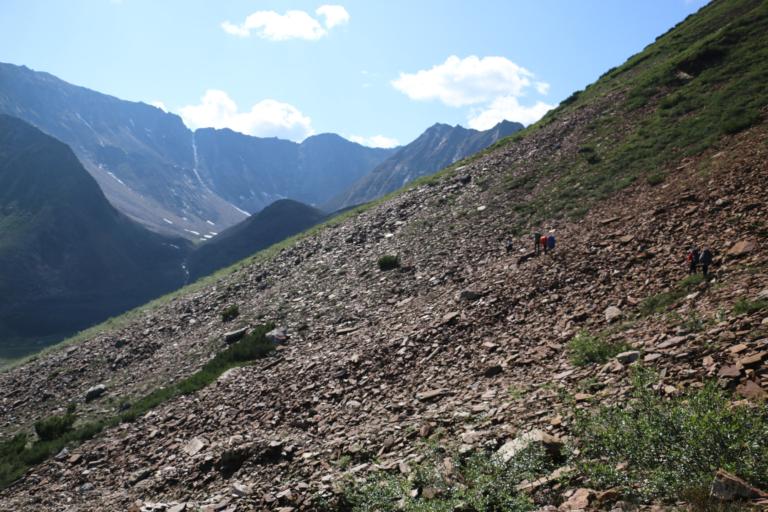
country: RU
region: Respublika Buryatiya
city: Novyy Uoyan
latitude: 56.2990
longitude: 111.2930
